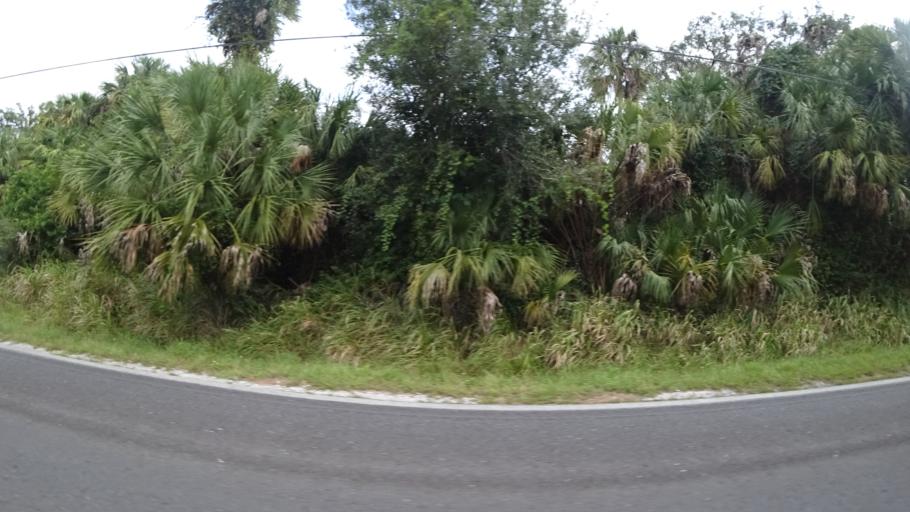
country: US
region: Florida
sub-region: Manatee County
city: Ellenton
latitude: 27.5648
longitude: -82.4789
